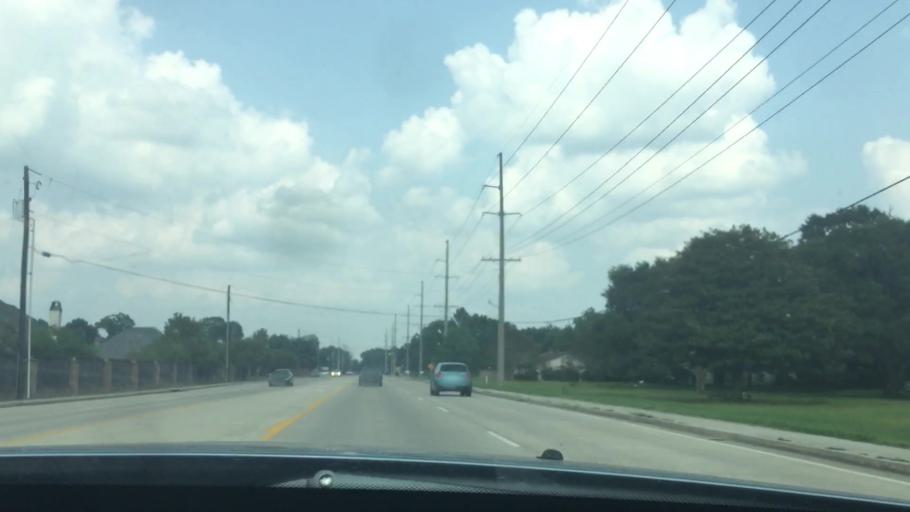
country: US
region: Louisiana
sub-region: East Baton Rouge Parish
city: Westminster
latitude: 30.4383
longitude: -91.0521
